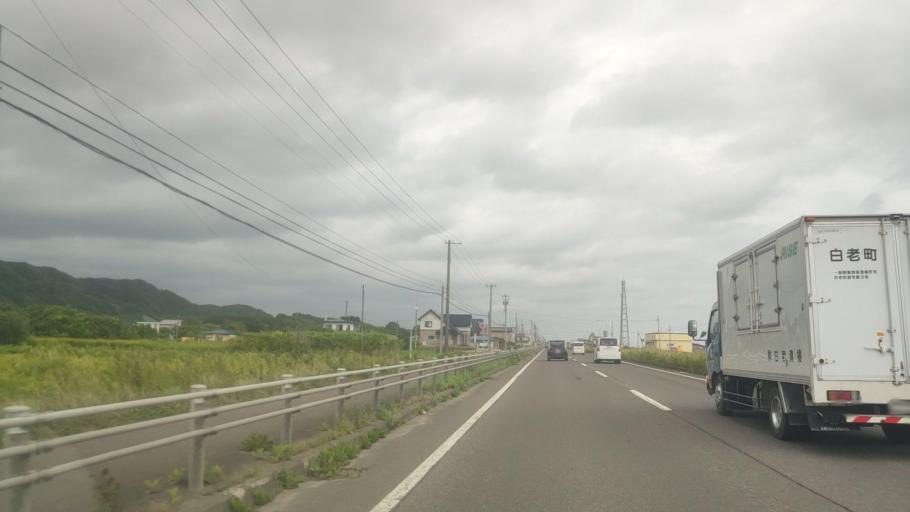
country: JP
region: Hokkaido
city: Shiraoi
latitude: 42.4669
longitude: 141.2249
